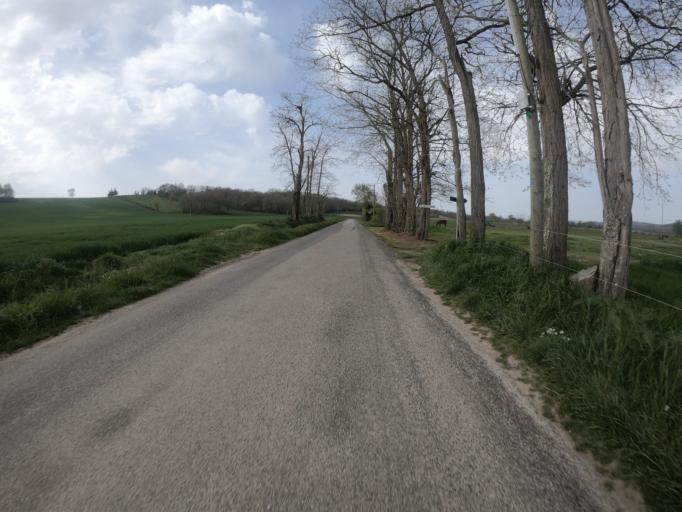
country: FR
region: Midi-Pyrenees
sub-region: Departement de l'Ariege
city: La Tour-du-Crieu
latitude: 43.1323
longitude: 1.7149
